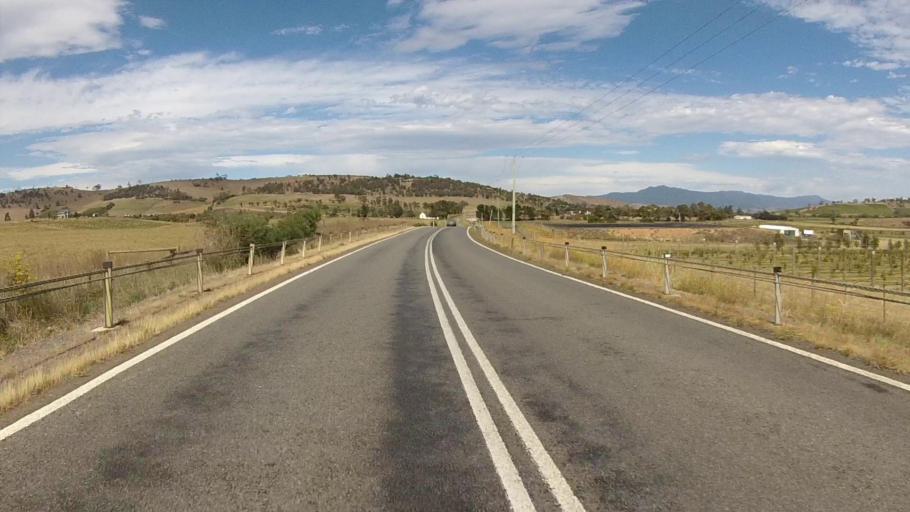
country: AU
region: Tasmania
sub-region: Brighton
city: Old Beach
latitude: -42.6889
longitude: 147.3498
